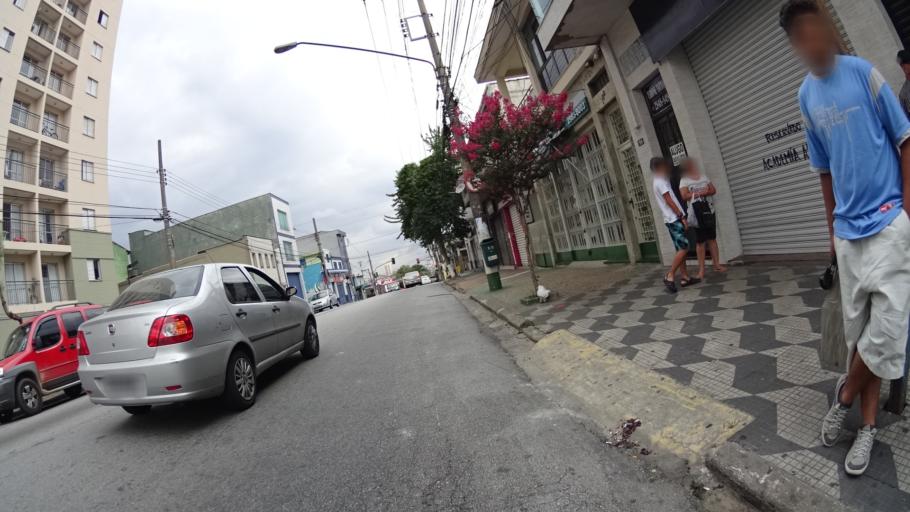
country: BR
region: Sao Paulo
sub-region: Guarulhos
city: Guarulhos
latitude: -23.4812
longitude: -46.6001
